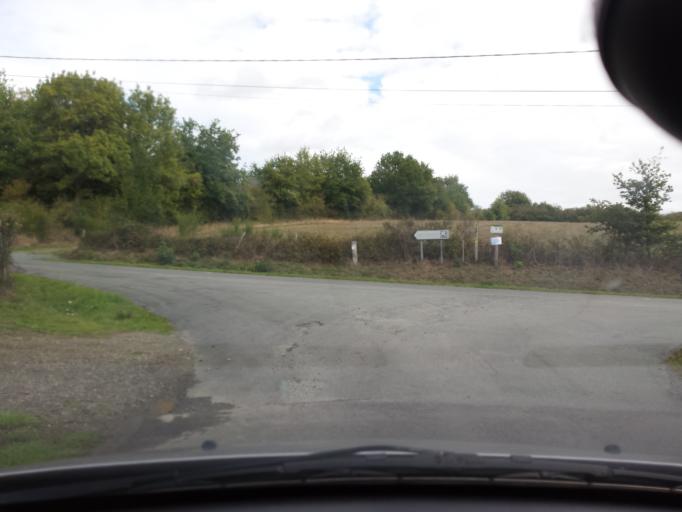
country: FR
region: Pays de la Loire
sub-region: Departement de la Vendee
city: Saint-Vincent-sur-Graon
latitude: 46.5176
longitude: -1.3821
